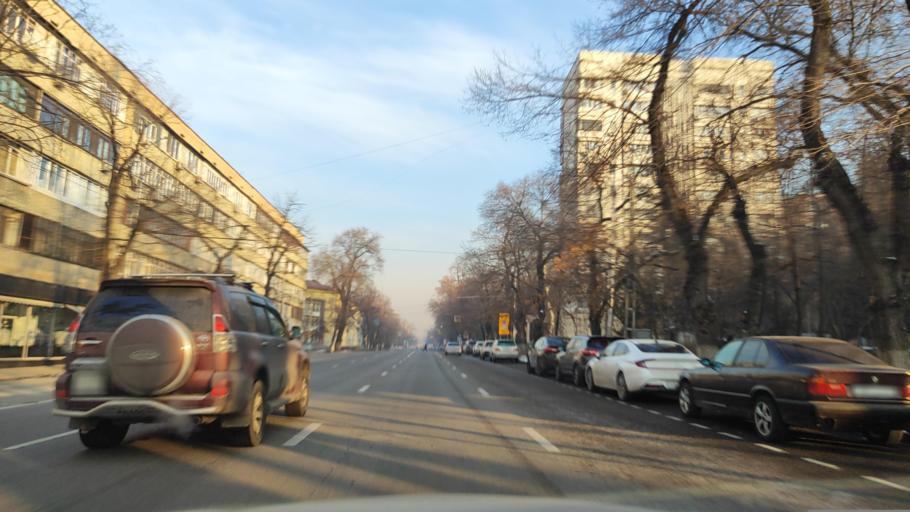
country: KZ
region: Almaty Qalasy
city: Almaty
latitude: 43.2501
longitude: 76.9512
